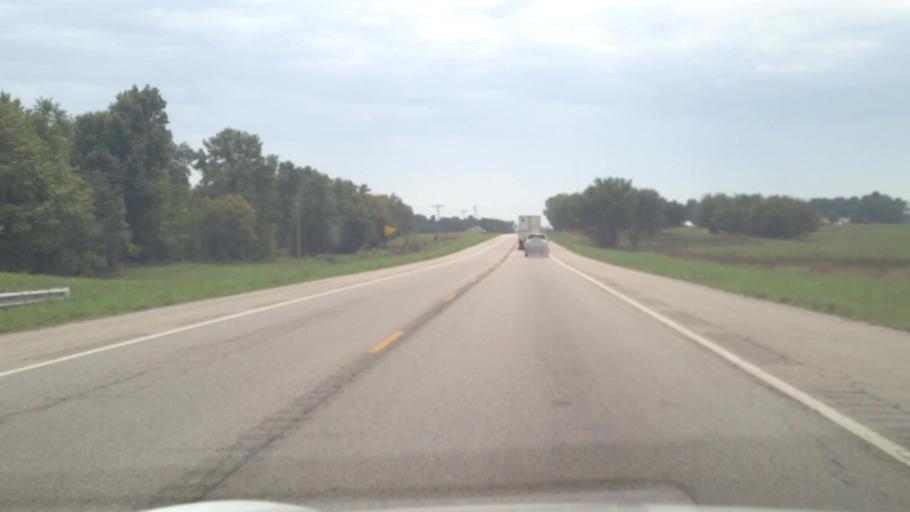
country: US
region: Kansas
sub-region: Crawford County
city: Pittsburg
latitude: 37.2550
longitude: -94.7052
